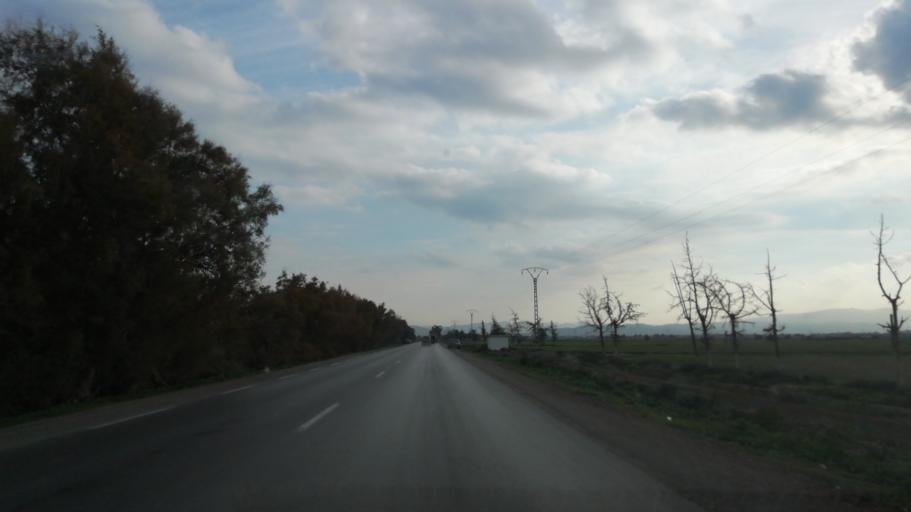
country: DZ
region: Mascara
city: Mascara
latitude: 35.6522
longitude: 0.0594
